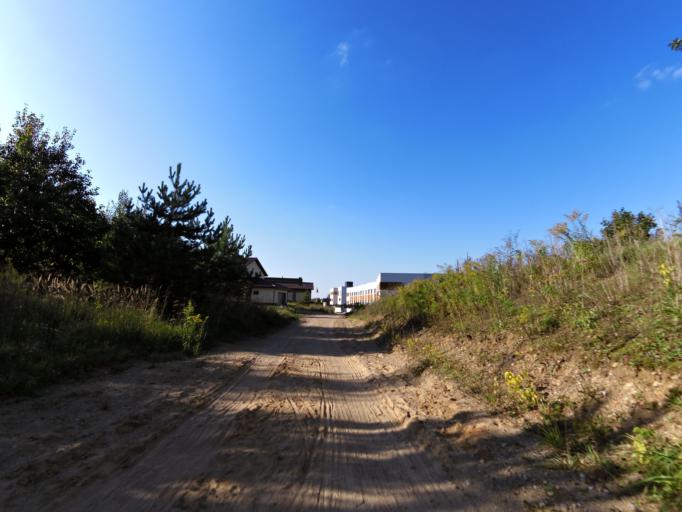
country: LT
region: Vilnius County
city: Pilaite
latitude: 54.7179
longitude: 25.1851
